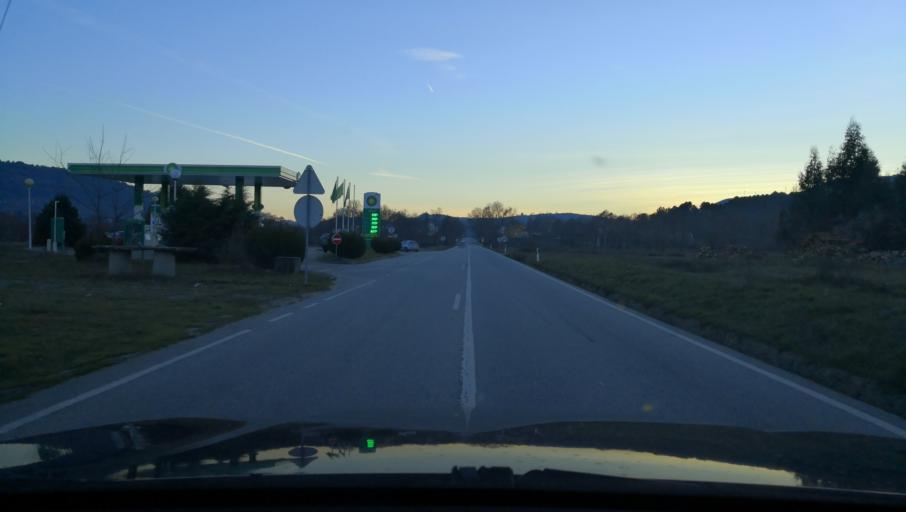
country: PT
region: Vila Real
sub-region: Vila Pouca de Aguiar
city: Vila Pouca de Aguiar
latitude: 41.4358
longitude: -7.6777
